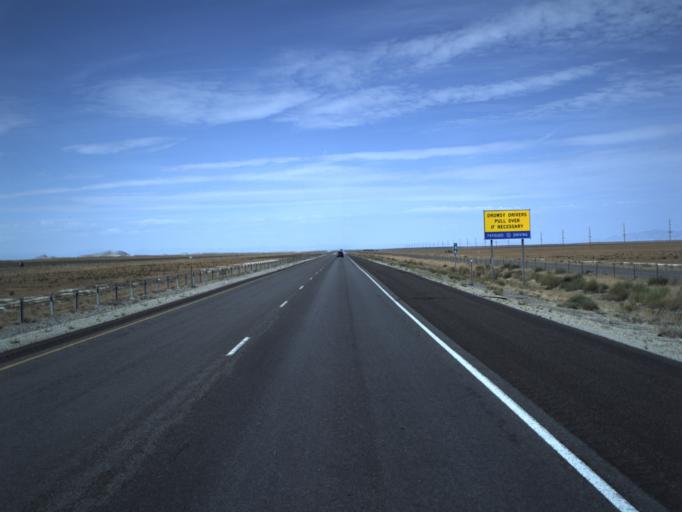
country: US
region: Utah
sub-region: Tooele County
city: Grantsville
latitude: 40.7263
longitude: -113.1676
